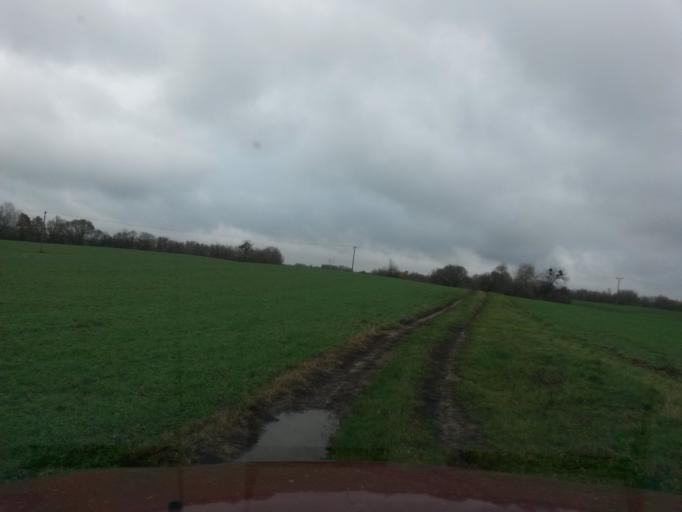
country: SK
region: Kosicky
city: Michalovce
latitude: 48.5555
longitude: 21.9318
